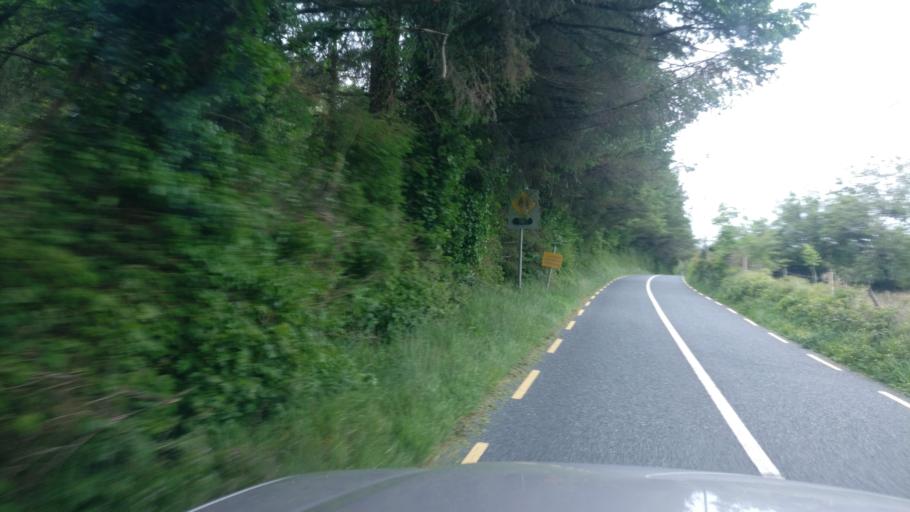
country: IE
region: Connaught
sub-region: County Galway
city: Loughrea
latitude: 53.0636
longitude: -8.6205
